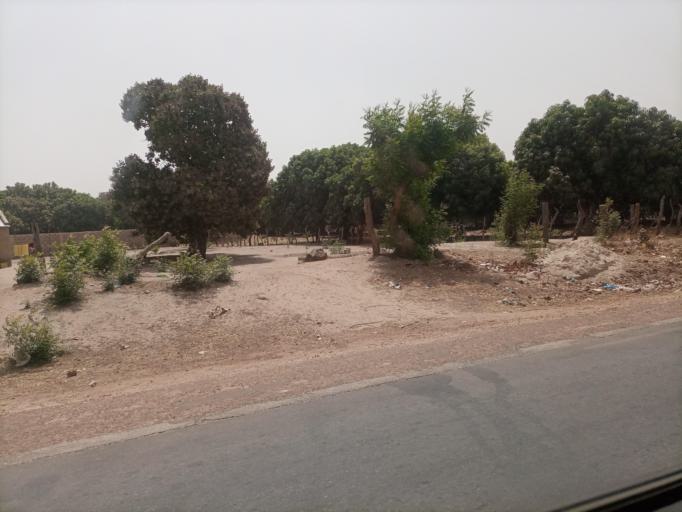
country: SN
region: Fatick
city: Sokone
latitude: 13.7238
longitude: -16.4244
